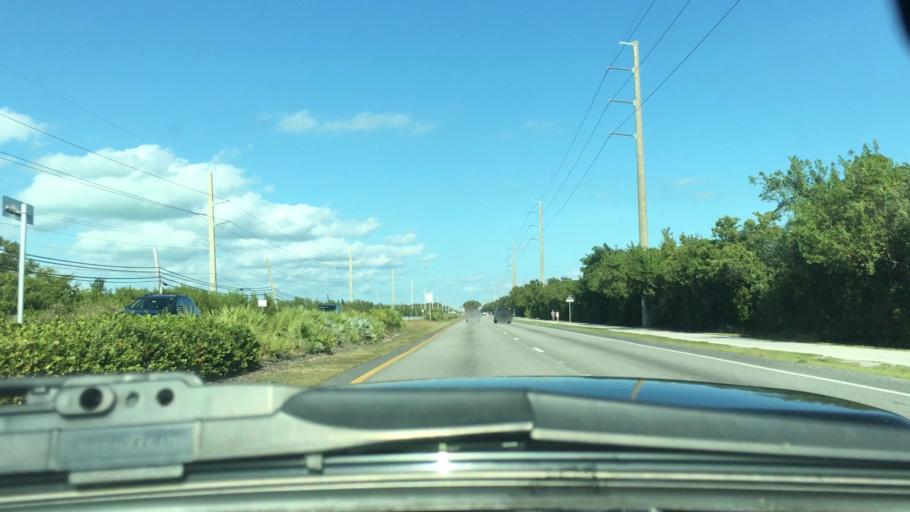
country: US
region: Florida
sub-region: Monroe County
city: Tavernier
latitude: 25.0272
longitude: -80.5071
